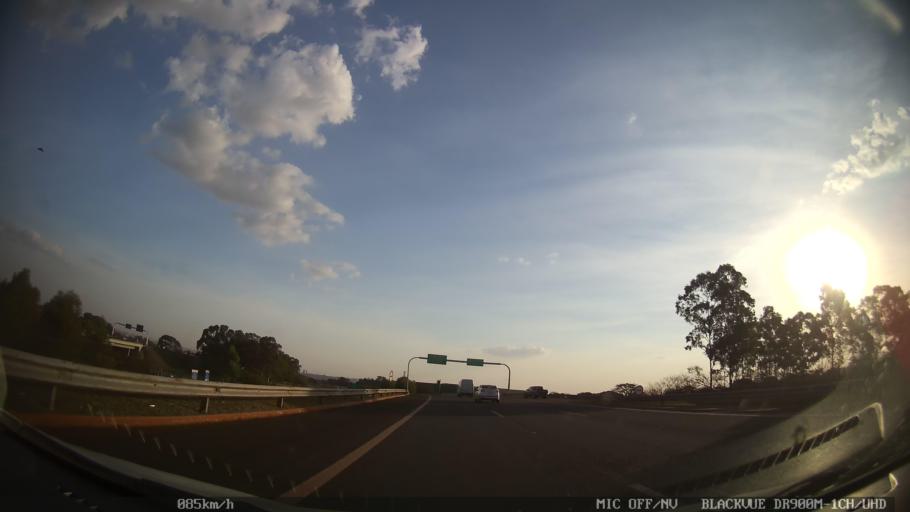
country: BR
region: Sao Paulo
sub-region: Ribeirao Preto
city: Ribeirao Preto
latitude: -21.1119
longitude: -47.7791
